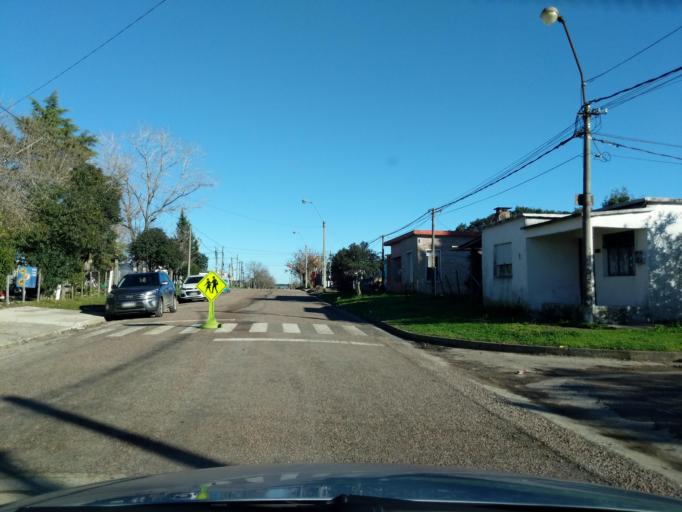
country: UY
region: Florida
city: Florida
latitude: -34.0960
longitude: -56.2376
